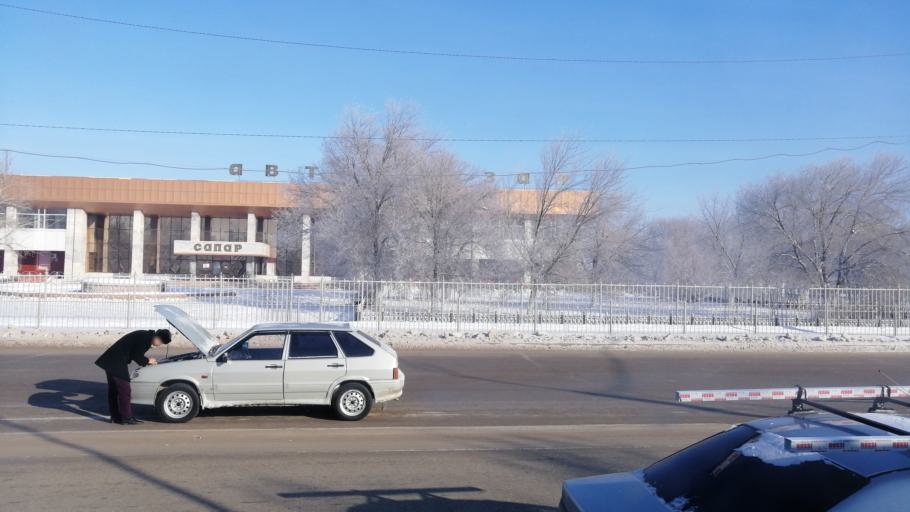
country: KZ
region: Aqtoebe
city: Aqtobe
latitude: 50.2929
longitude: 57.1987
